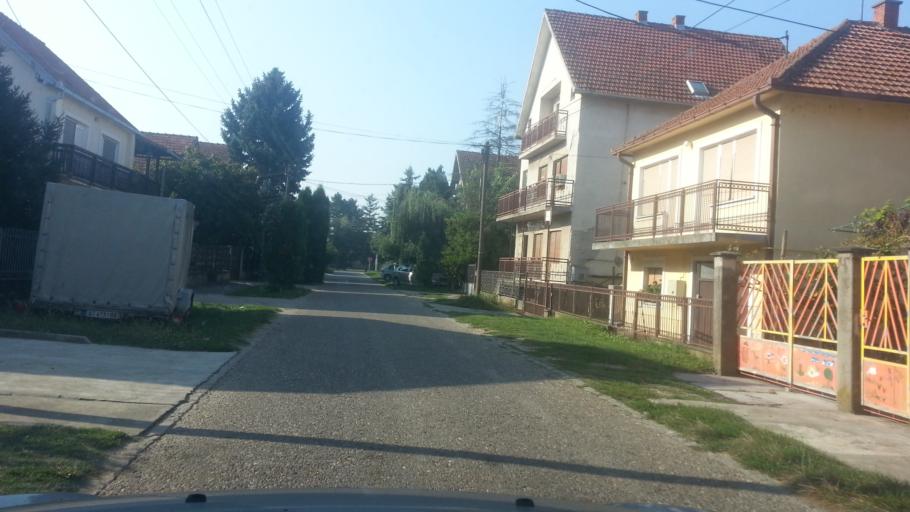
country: RS
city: Novi Banovci
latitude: 44.9580
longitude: 20.2832
